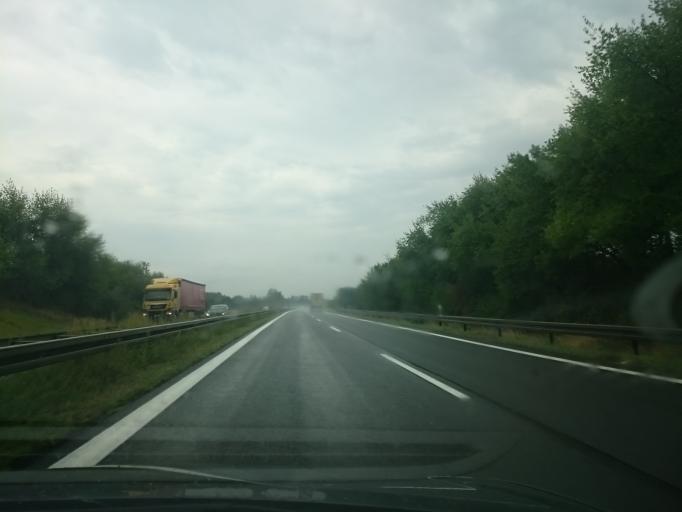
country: DE
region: Brandenburg
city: Brieselang
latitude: 52.6574
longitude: 13.0033
